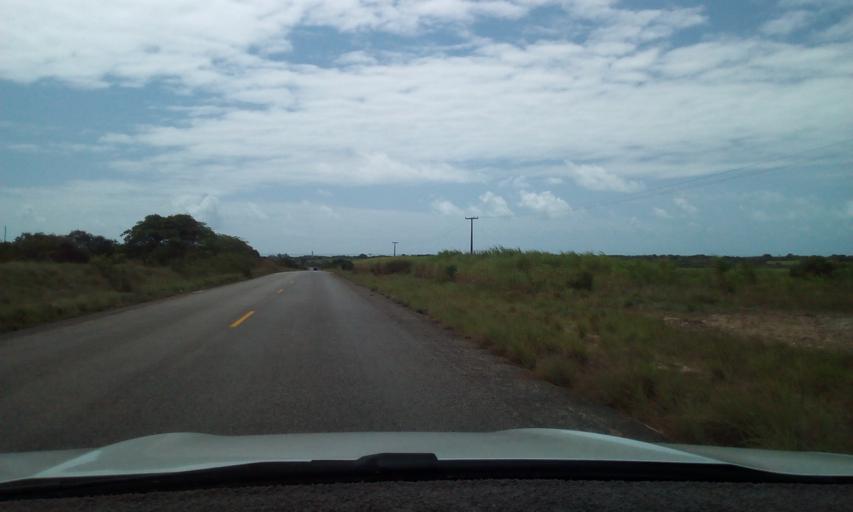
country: BR
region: Paraiba
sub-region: Rio Tinto
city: Rio Tinto
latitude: -6.7423
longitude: -34.9676
